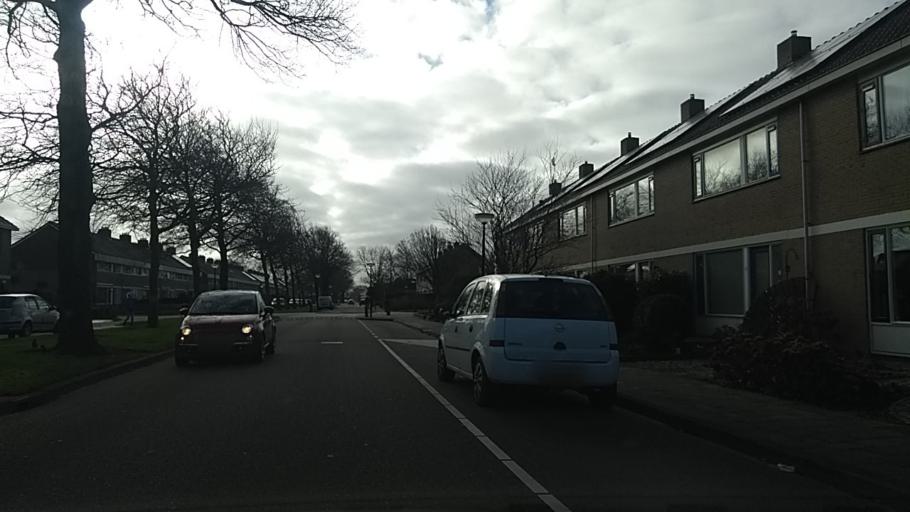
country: NL
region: Friesland
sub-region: Gemeente Harlingen
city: Harlingen
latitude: 53.1682
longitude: 5.4387
